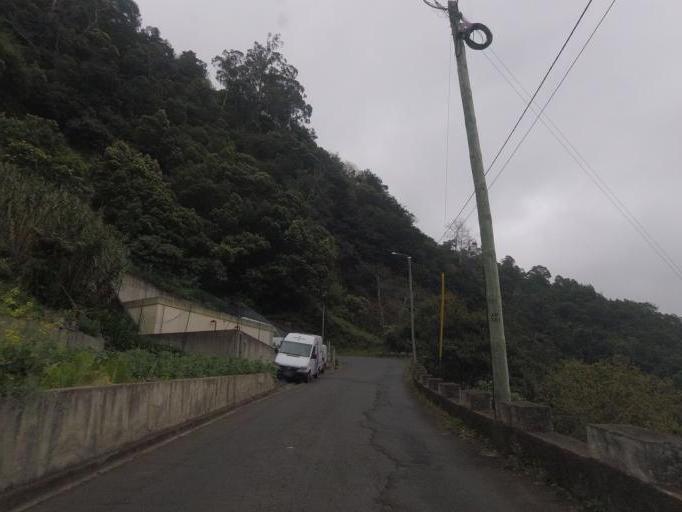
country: PT
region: Madeira
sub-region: Santa Cruz
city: Santa Cruz
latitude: 32.7368
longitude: -16.8101
